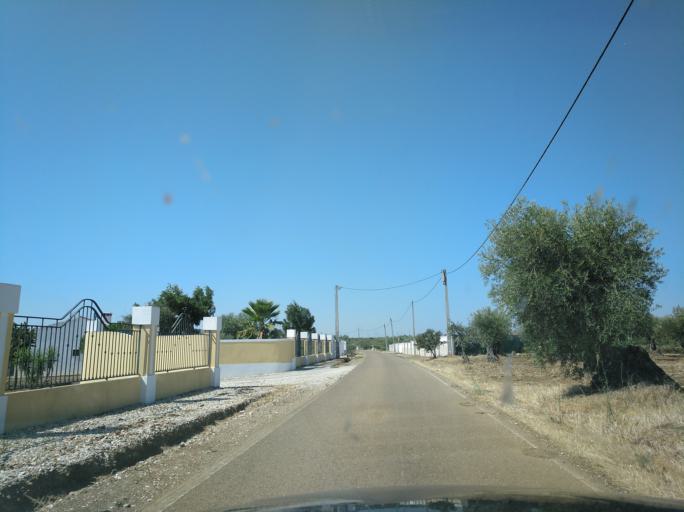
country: PT
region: Portalegre
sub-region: Campo Maior
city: Campo Maior
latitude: 39.0361
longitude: -7.0348
